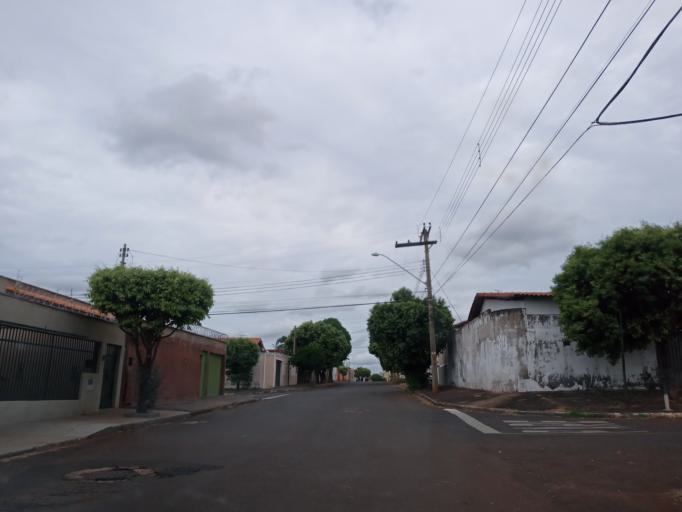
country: BR
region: Minas Gerais
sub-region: Ituiutaba
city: Ituiutaba
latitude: -18.9706
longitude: -49.4741
